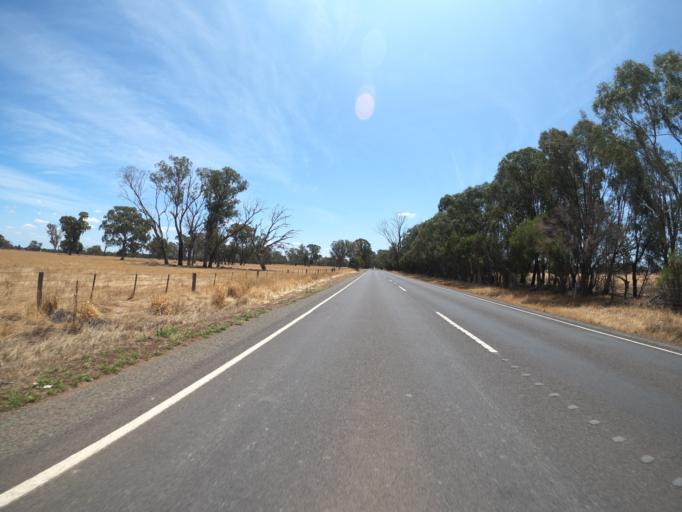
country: AU
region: Victoria
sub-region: Benalla
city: Benalla
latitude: -36.5070
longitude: 146.0261
